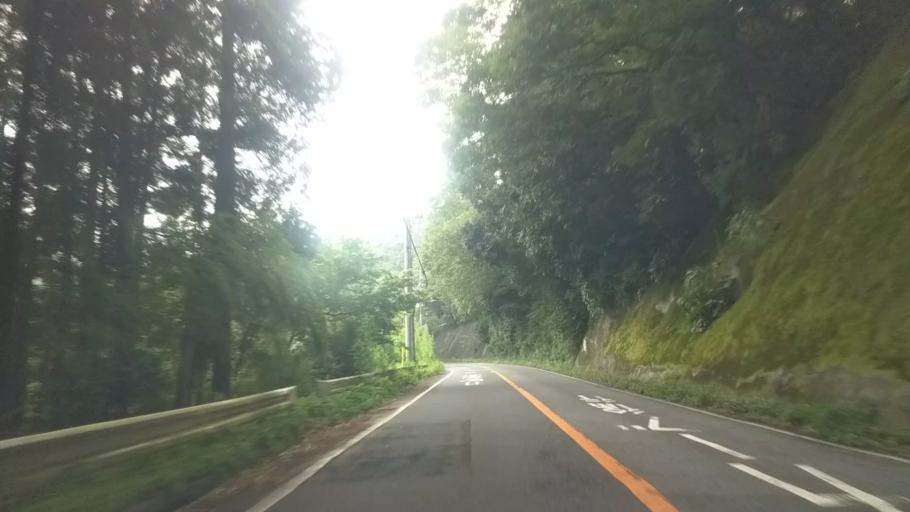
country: JP
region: Chiba
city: Kawaguchi
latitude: 35.2426
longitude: 140.0764
